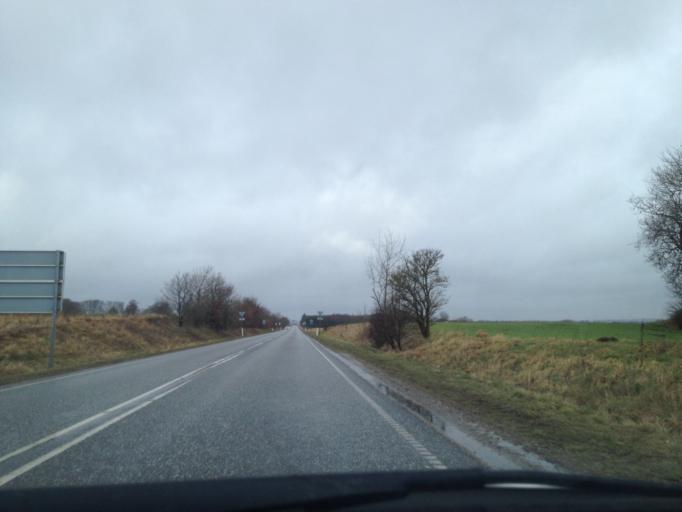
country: DK
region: South Denmark
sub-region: Kolding Kommune
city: Vamdrup
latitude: 55.4229
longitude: 9.3083
